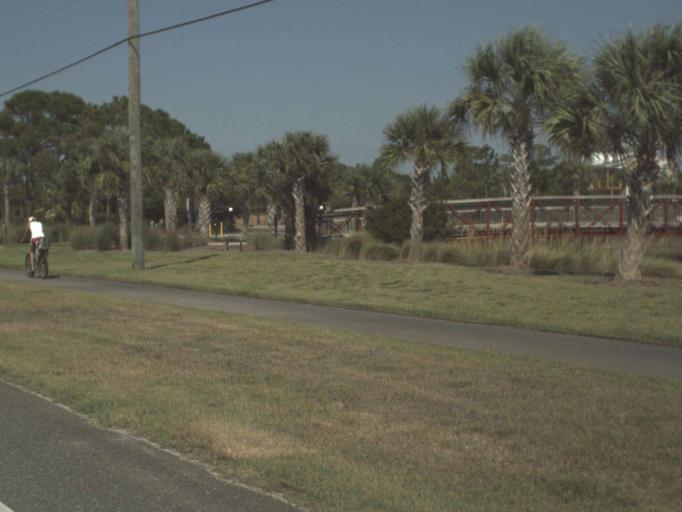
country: US
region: Florida
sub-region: Gulf County
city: Port Saint Joe
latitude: 29.7352
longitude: -85.3926
